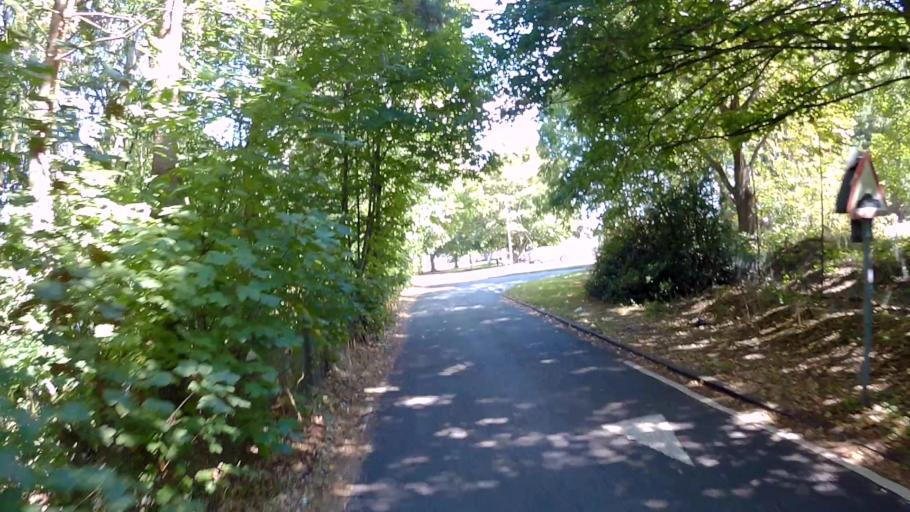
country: GB
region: England
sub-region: Bracknell Forest
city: Crowthorne
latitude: 51.3938
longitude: -0.7813
